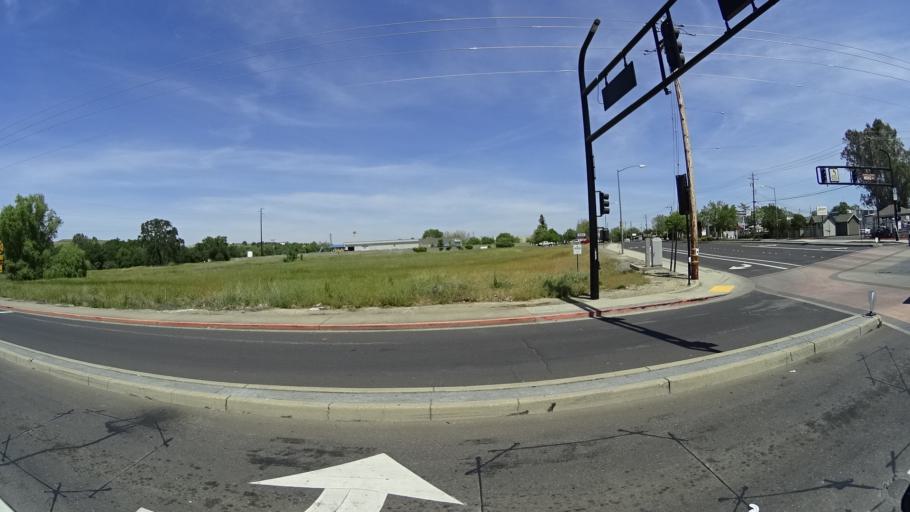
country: US
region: California
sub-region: Placer County
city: Rocklin
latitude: 38.7953
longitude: -121.2327
